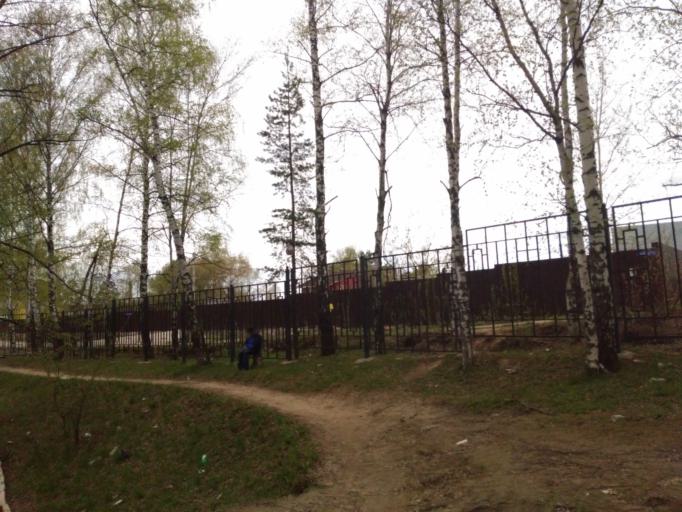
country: RU
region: Moskovskaya
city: Nakhabino
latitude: 55.8468
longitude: 37.1660
